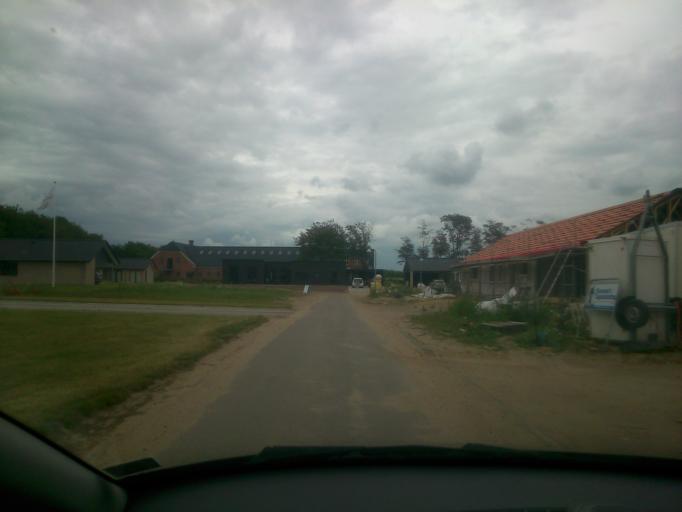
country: DK
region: South Denmark
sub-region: Esbjerg Kommune
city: Esbjerg
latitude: 55.5278
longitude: 8.4301
